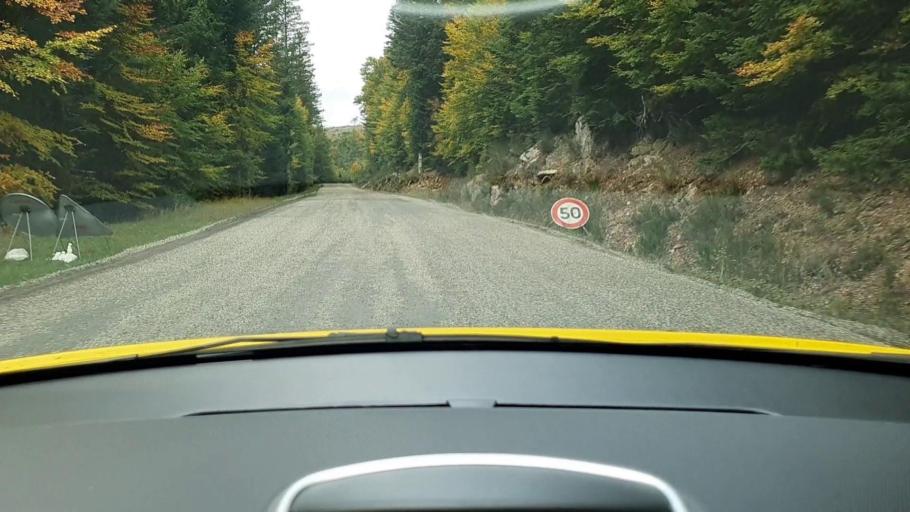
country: FR
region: Languedoc-Roussillon
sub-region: Departement du Gard
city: Valleraugue
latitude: 44.0681
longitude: 3.5437
